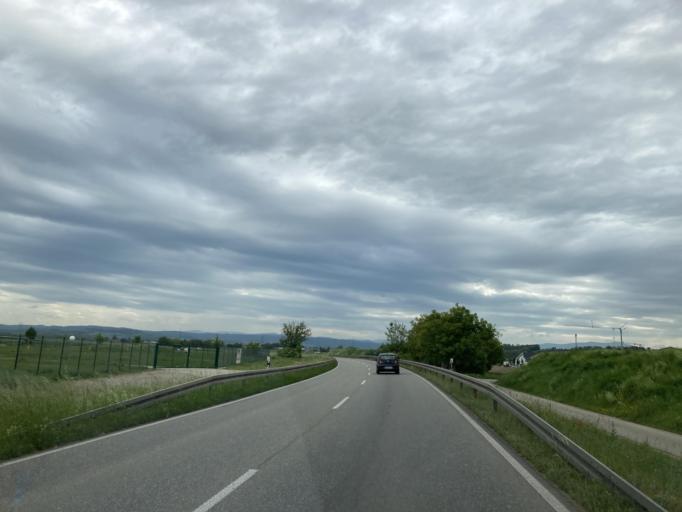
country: DE
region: Baden-Wuerttemberg
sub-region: Freiburg Region
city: Endingen
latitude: 48.1515
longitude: 7.7039
